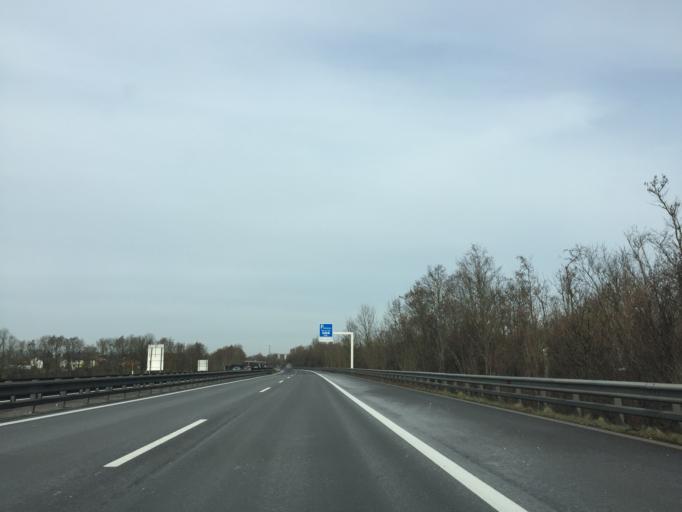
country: AT
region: Upper Austria
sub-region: Politischer Bezirk Ried im Innkreis
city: Ried im Innkreis
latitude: 48.2553
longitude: 13.5139
